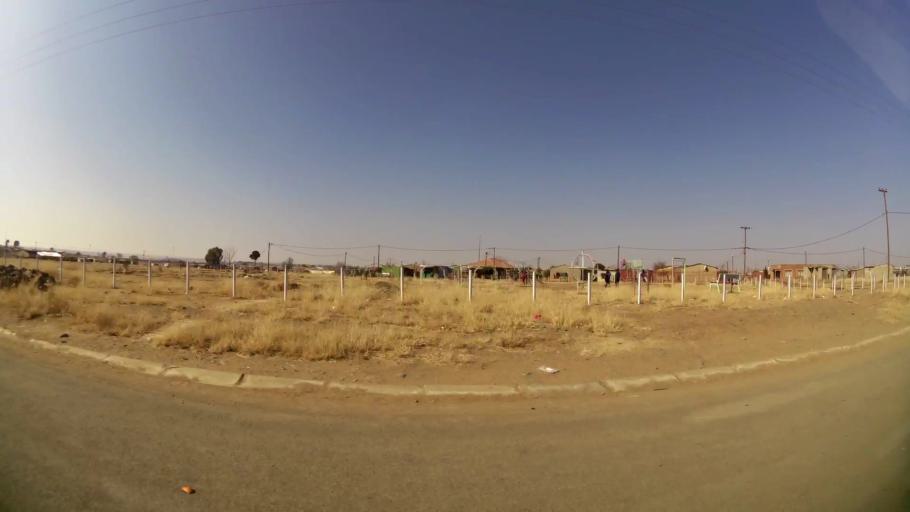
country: ZA
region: Orange Free State
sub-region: Mangaung Metropolitan Municipality
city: Bloemfontein
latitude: -29.1968
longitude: 26.2593
